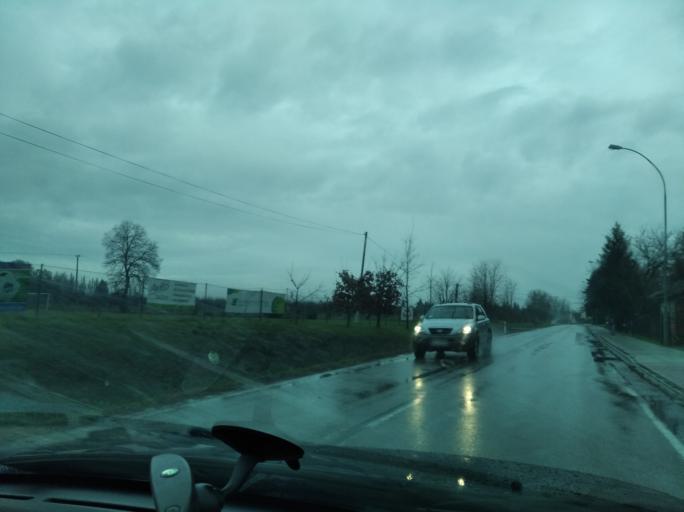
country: PL
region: Subcarpathian Voivodeship
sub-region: Powiat lancucki
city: Albigowa
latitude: 50.0271
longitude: 22.2264
